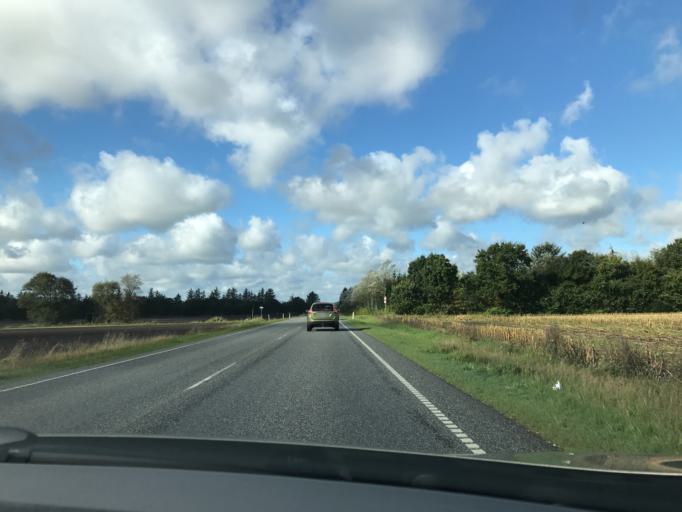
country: DK
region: South Denmark
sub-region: Billund Kommune
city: Billund
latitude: 55.7203
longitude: 9.1628
